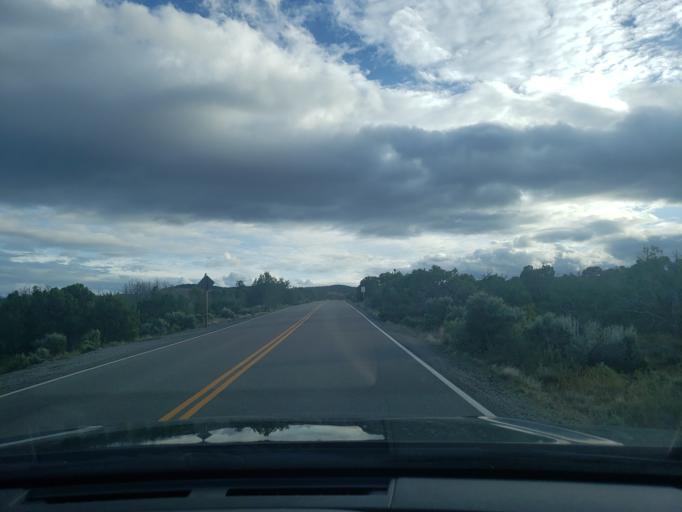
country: US
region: Colorado
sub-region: Mesa County
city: Redlands
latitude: 39.0332
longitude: -108.6506
